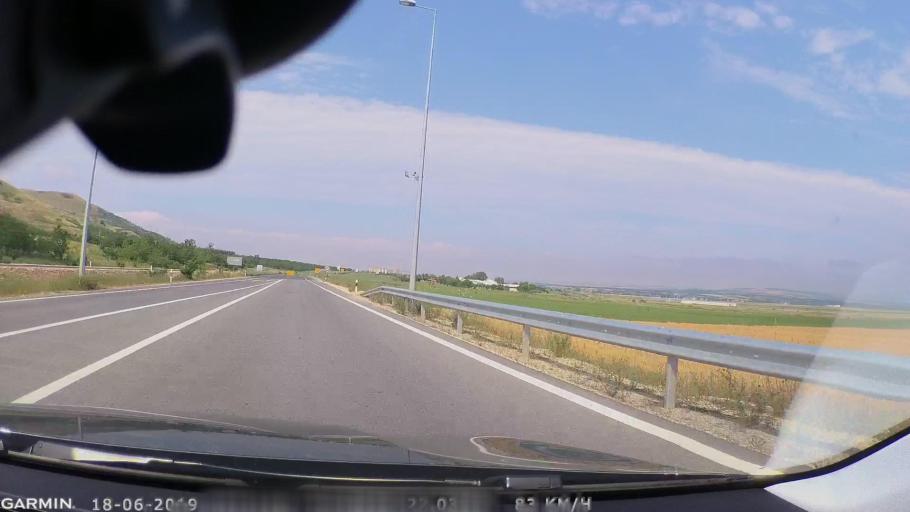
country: MK
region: Sveti Nikole
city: Sveti Nikole
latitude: 41.8283
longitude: 22.0024
